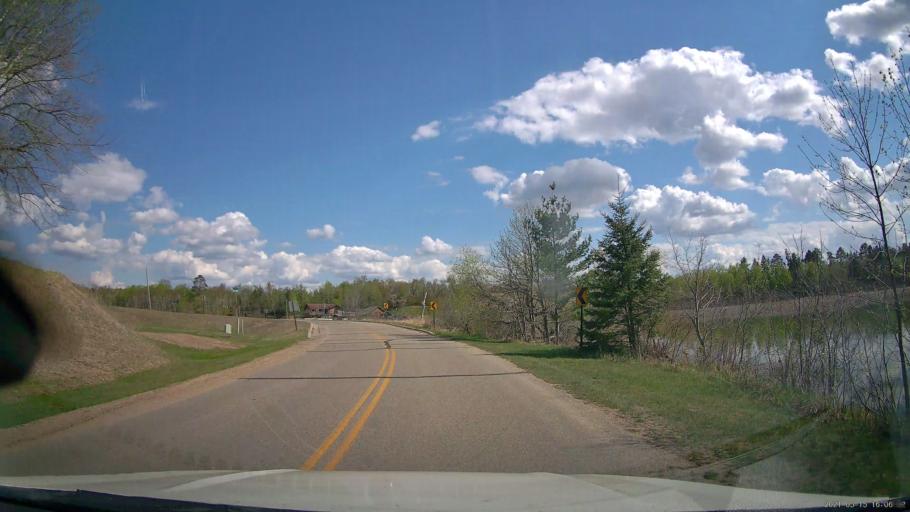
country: US
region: Minnesota
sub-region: Hubbard County
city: Park Rapids
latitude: 46.9800
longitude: -94.9516
